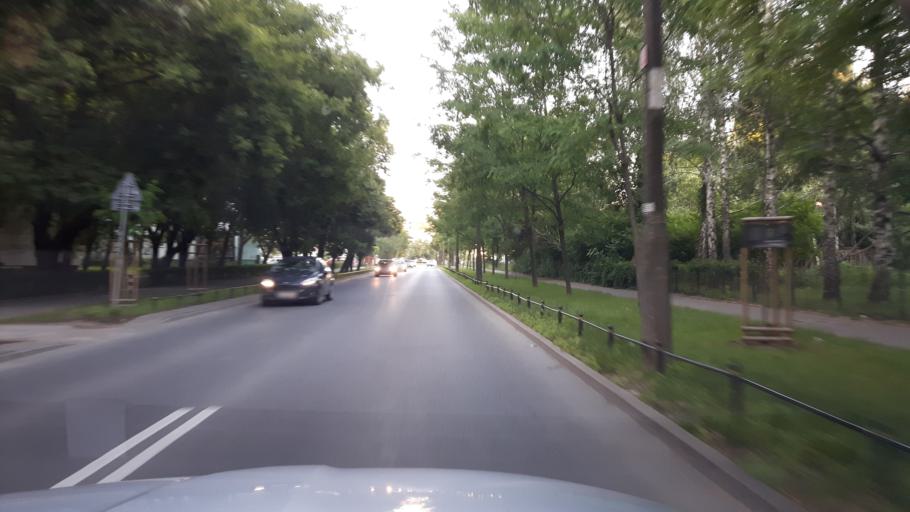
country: PL
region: Masovian Voivodeship
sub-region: Warszawa
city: Ursynow
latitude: 52.1746
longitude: 21.0589
